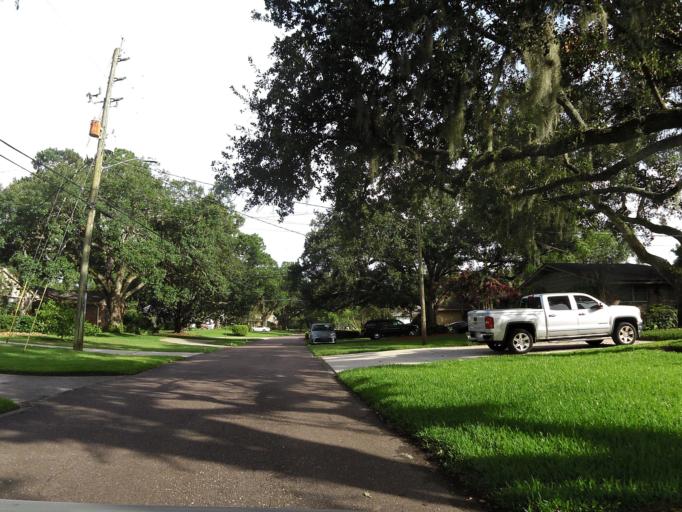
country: US
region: Florida
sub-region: Clay County
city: Bellair-Meadowbrook Terrace
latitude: 30.2598
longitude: -81.7098
